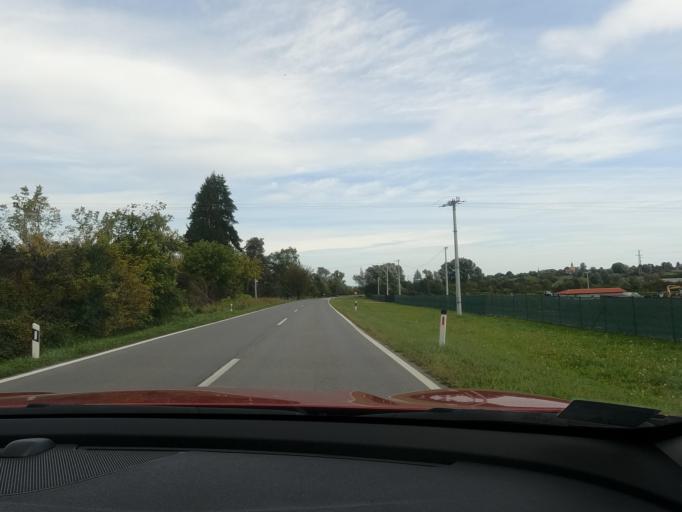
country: HR
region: Sisacko-Moslavacka
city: Osekovo
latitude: 45.5256
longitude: 16.5387
